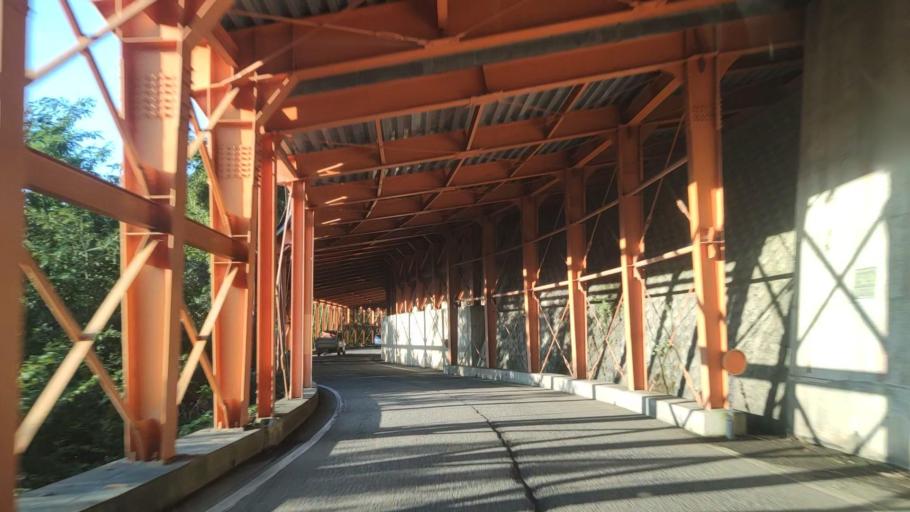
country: JP
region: Toyama
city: Yatsuomachi-higashikumisaka
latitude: 36.5217
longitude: 137.0286
